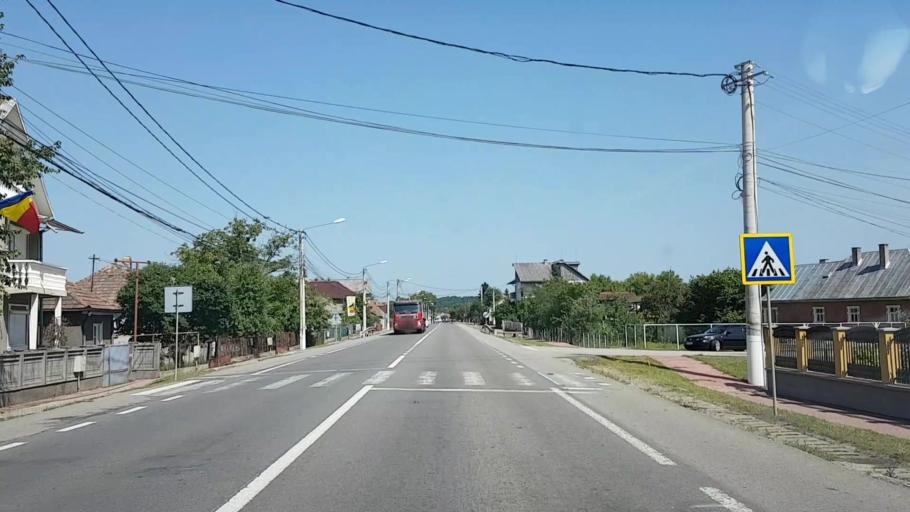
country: RO
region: Bistrita-Nasaud
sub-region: Comuna Beclean
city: Beclean
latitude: 47.1755
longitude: 24.1579
